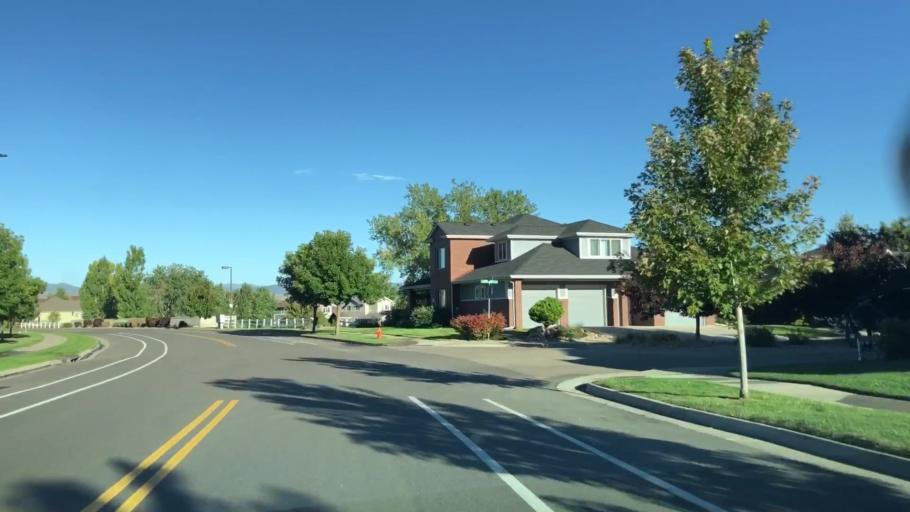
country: US
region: Colorado
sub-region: Larimer County
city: Loveland
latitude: 40.4536
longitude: -105.0284
